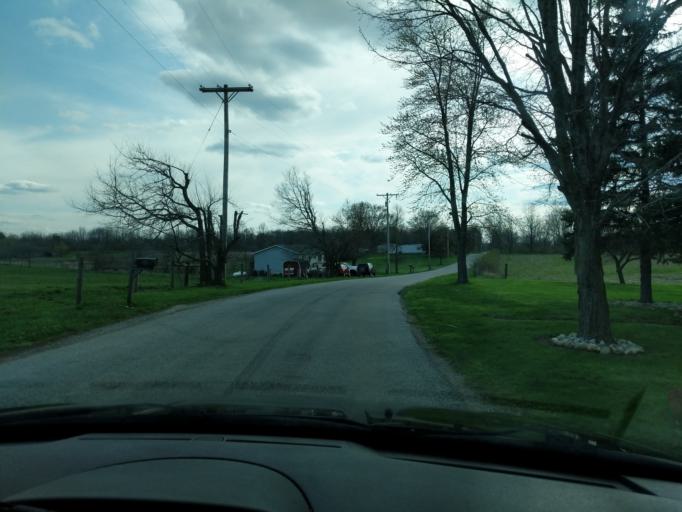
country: US
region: Ohio
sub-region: Champaign County
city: Urbana
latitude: 40.1334
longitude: -83.6563
